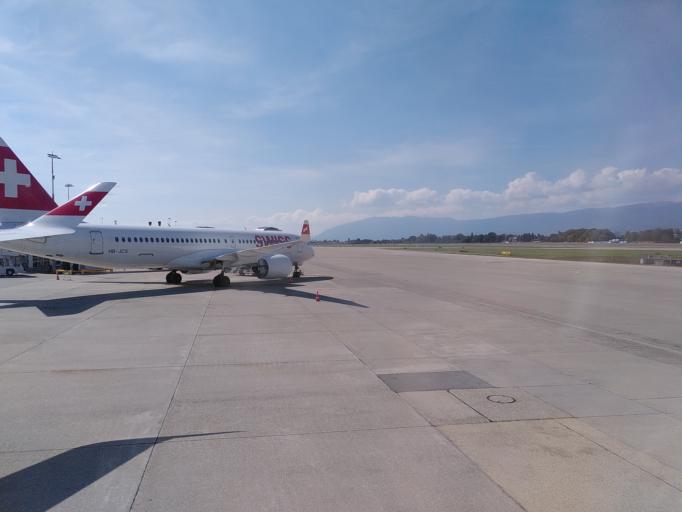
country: CH
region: Geneva
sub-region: Geneva
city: Les Avanchets
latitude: 46.2326
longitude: 6.1056
